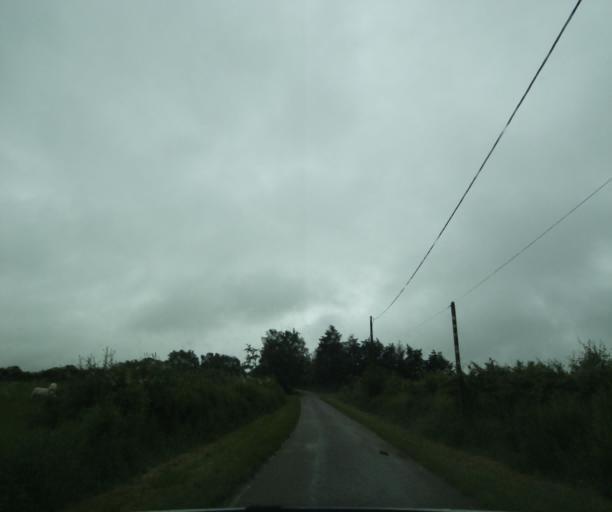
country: FR
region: Bourgogne
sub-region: Departement de Saone-et-Loire
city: Paray-le-Monial
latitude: 46.4735
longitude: 4.1960
